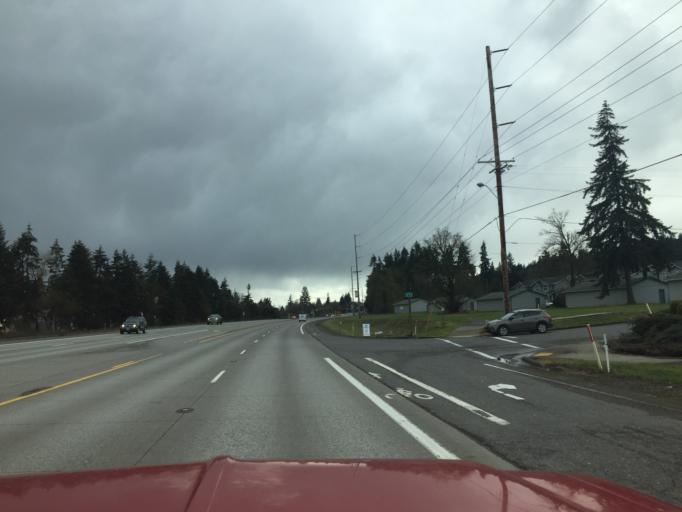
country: US
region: Oregon
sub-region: Columbia County
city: Columbia City
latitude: 45.8975
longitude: -122.8133
